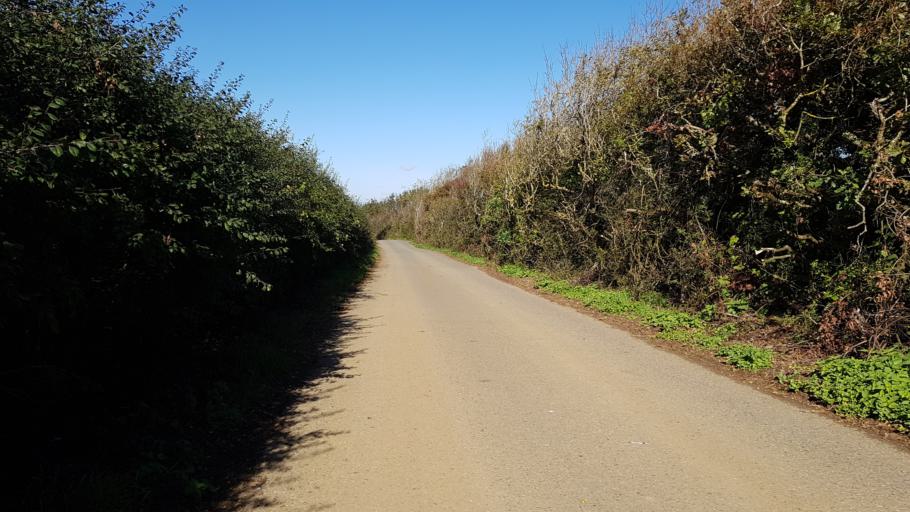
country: GB
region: England
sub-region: Isle of Wight
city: Newport
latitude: 50.6847
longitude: -1.2807
